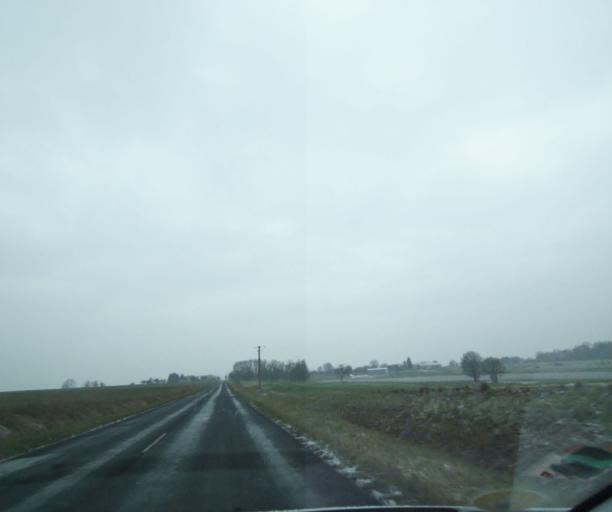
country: FR
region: Champagne-Ardenne
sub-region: Departement de la Haute-Marne
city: Wassy
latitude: 48.4655
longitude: 5.0289
